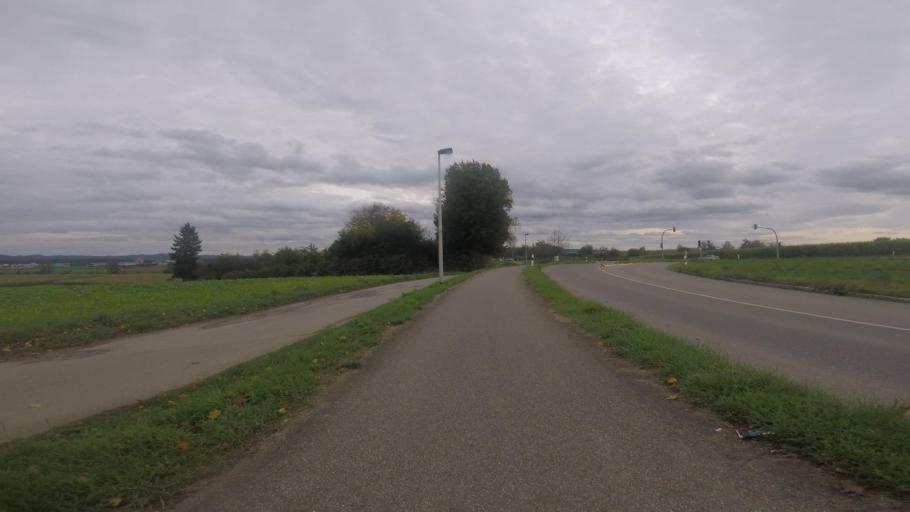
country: DE
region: Baden-Wuerttemberg
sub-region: Regierungsbezirk Stuttgart
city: Aspach
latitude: 48.9613
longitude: 9.4050
